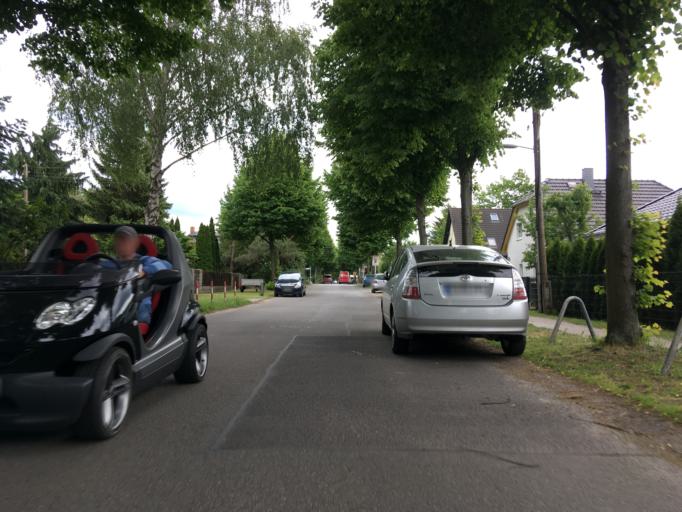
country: DE
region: Berlin
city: Kaulsdorf
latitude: 52.4871
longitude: 13.5813
